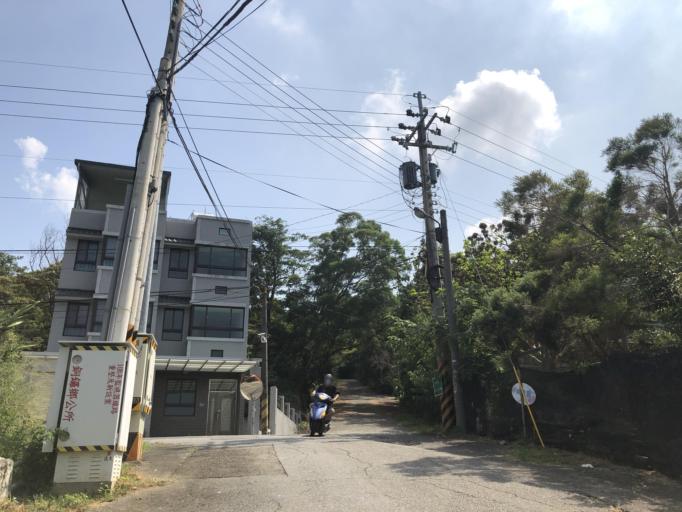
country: TW
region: Taiwan
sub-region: Miaoli
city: Miaoli
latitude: 24.4728
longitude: 120.7939
